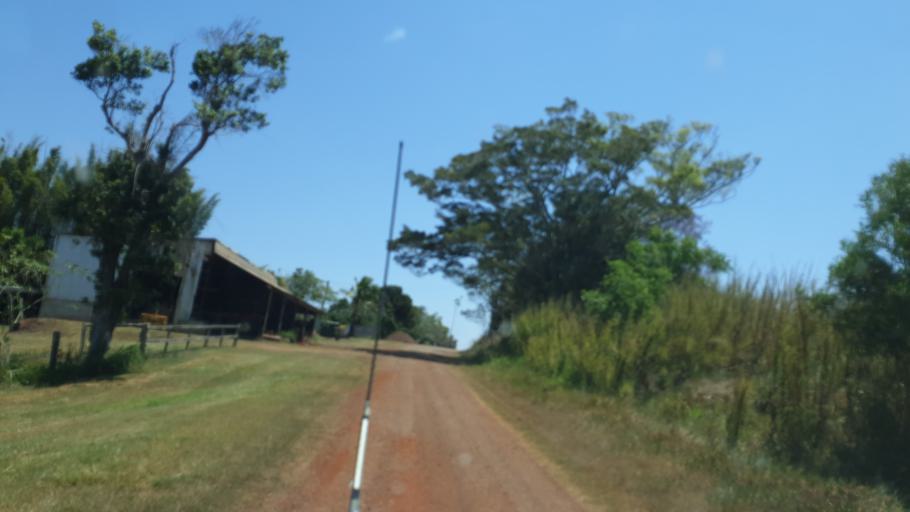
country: AU
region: Queensland
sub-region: Tablelands
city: Atherton
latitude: -17.3481
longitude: 145.6220
